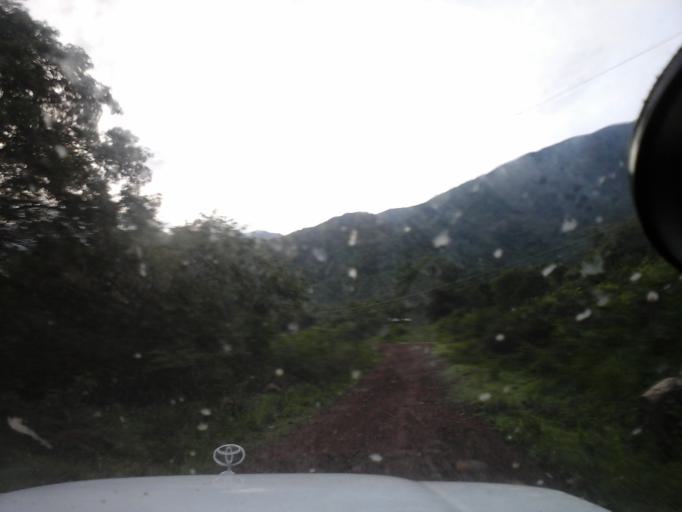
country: CO
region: Cesar
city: Agustin Codazzi
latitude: 10.1713
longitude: -73.1624
